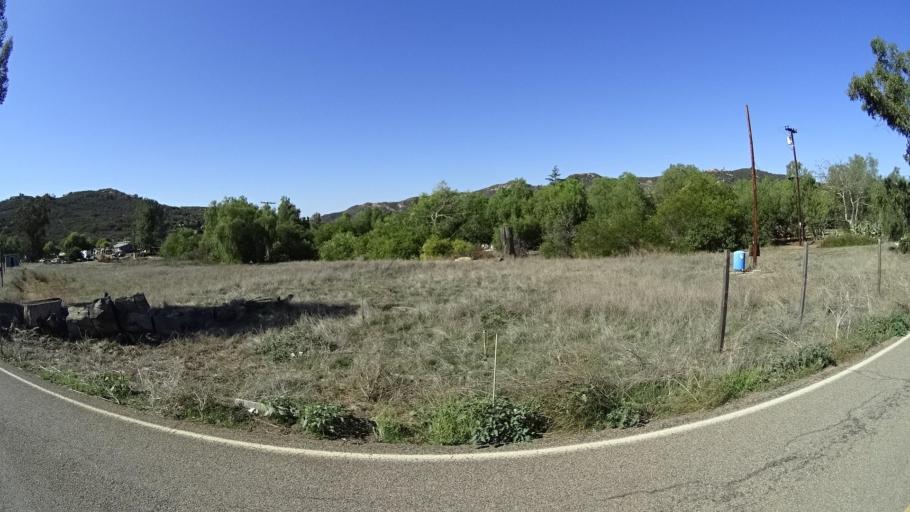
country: US
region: California
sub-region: San Diego County
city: Jamul
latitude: 32.7204
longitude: -116.8043
